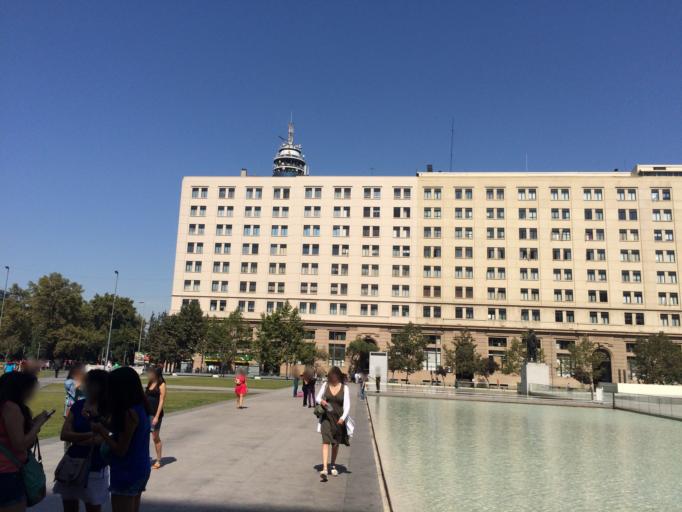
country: CL
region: Santiago Metropolitan
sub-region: Provincia de Santiago
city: Santiago
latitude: -33.4437
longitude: -70.6532
